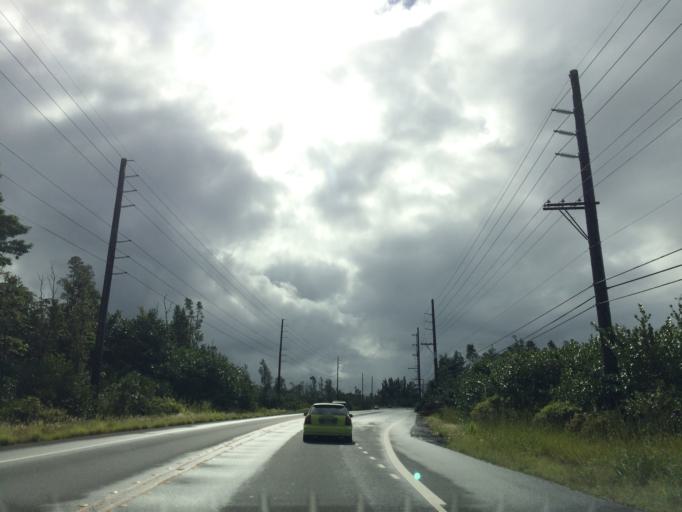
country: US
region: Hawaii
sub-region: Hawaii County
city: Ainaloa
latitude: 19.5451
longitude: -154.9764
